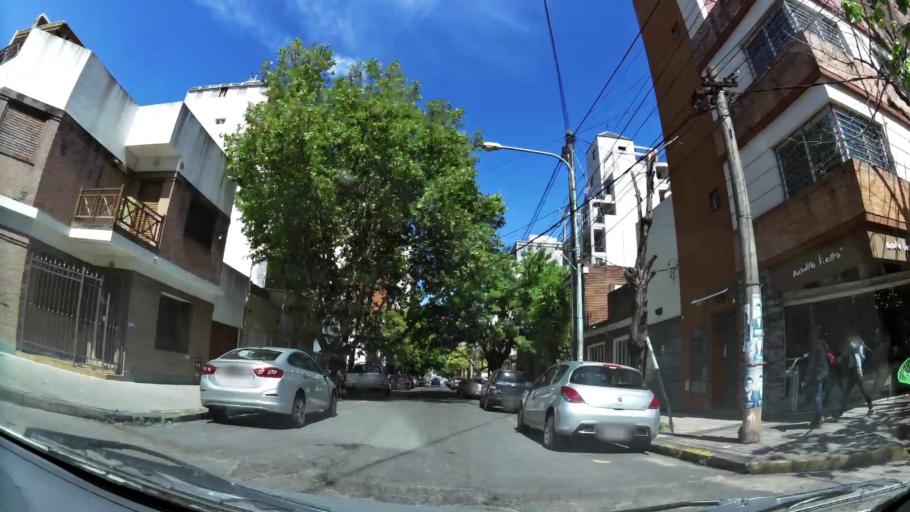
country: AR
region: Buenos Aires
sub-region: Partido de Quilmes
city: Quilmes
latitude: -34.7198
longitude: -58.2591
